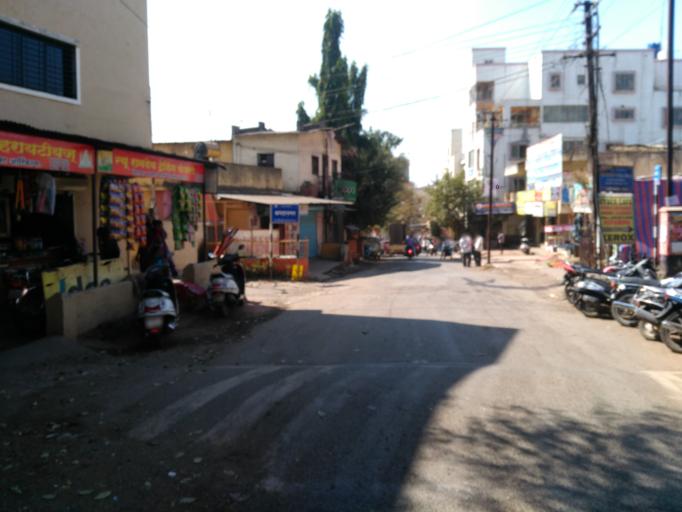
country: IN
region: Maharashtra
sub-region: Pune Division
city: Pune
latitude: 18.4568
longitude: 73.8894
